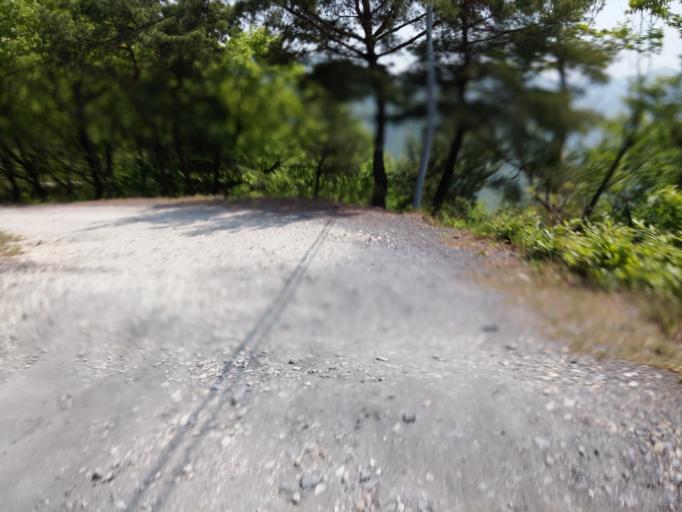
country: KR
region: Chungcheongbuk-do
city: Okcheon
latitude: 36.4167
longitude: 127.5930
